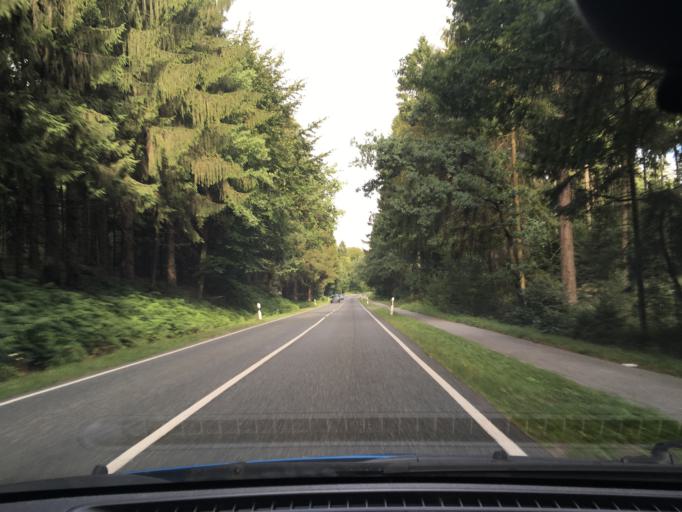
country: DE
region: Lower Saxony
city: Buchholz in der Nordheide
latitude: 53.4047
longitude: 9.8687
